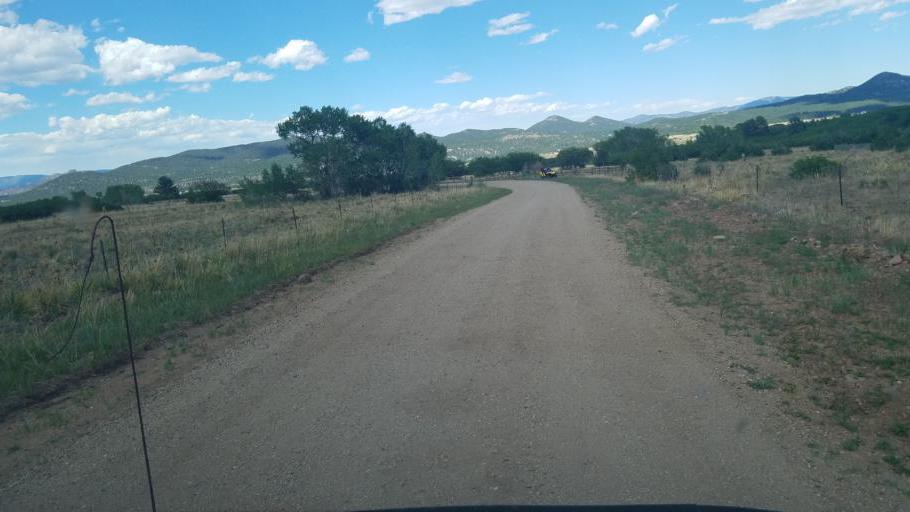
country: US
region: Colorado
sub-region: Custer County
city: Westcliffe
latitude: 38.2243
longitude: -105.6002
